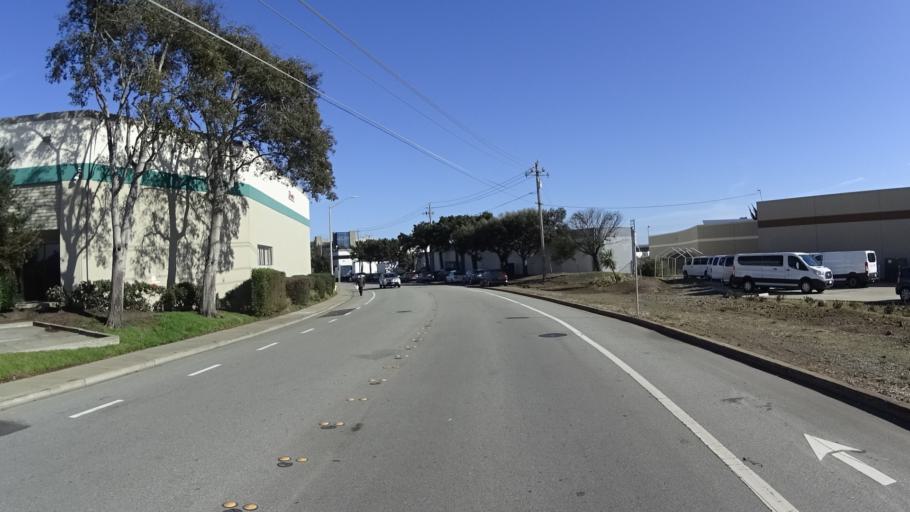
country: US
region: California
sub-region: San Mateo County
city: South San Francisco
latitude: 37.6510
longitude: -122.3869
